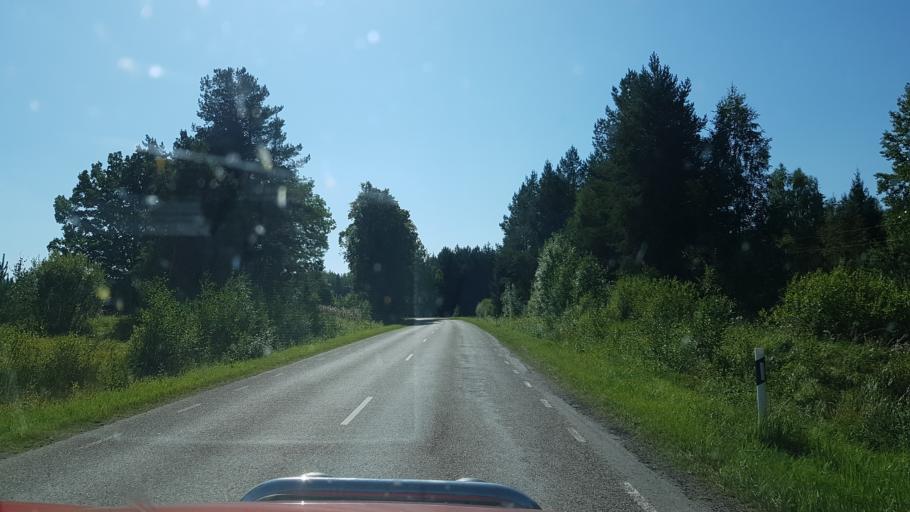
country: EE
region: Polvamaa
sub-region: Polva linn
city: Polva
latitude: 58.2528
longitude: 27.1826
